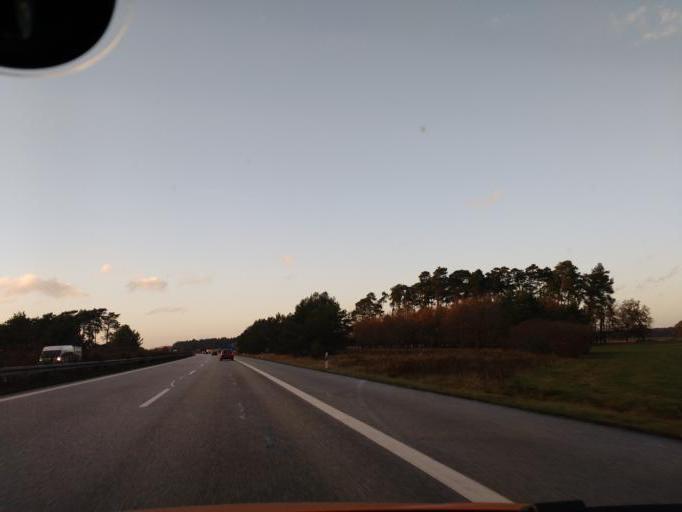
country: DE
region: Mecklenburg-Vorpommern
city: Sulstorf
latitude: 53.4588
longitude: 11.3507
